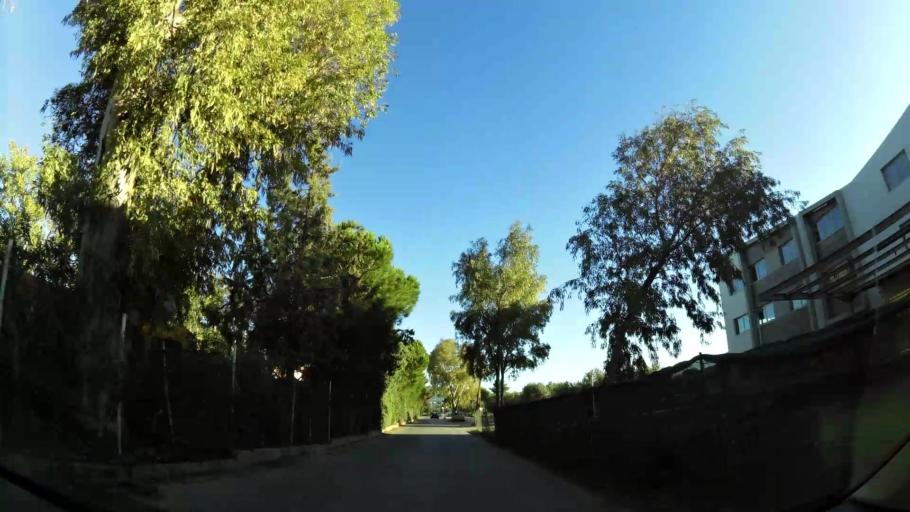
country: GR
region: Attica
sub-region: Nomarchia Anatolikis Attikis
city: Pallini
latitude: 37.9992
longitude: 23.8658
